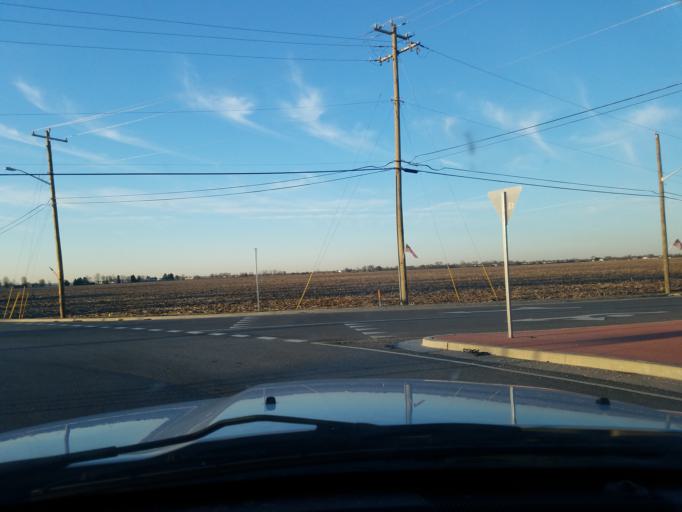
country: US
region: Indiana
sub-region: Johnson County
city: Whiteland
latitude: 39.5506
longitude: -86.0593
